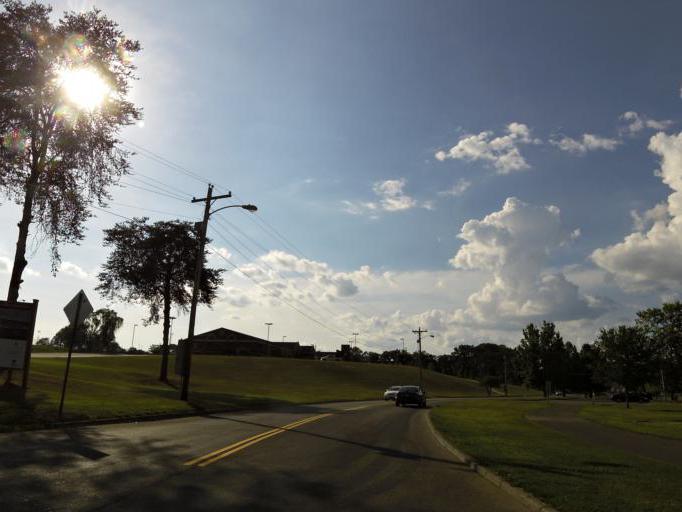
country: US
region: Tennessee
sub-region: Blount County
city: Alcoa
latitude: 35.7904
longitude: -83.9764
